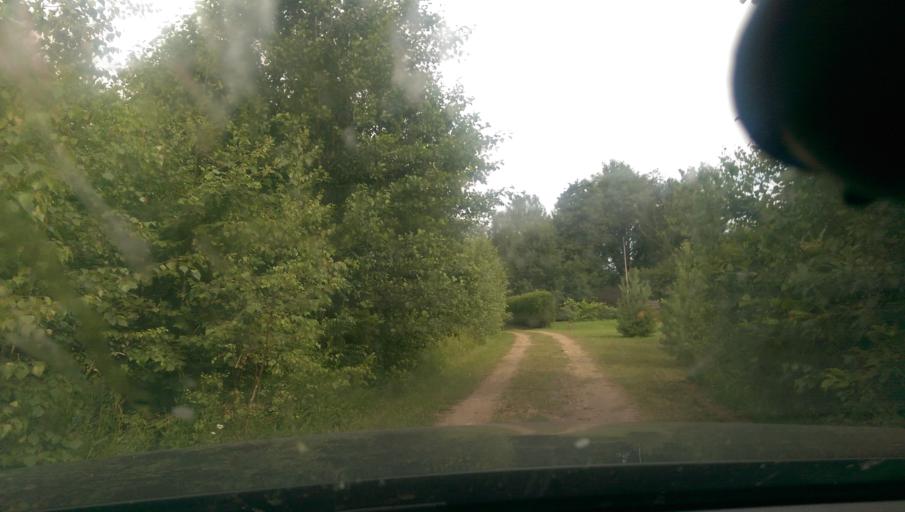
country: LT
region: Klaipedos apskritis
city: Gargzdai
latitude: 55.6529
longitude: 21.3352
